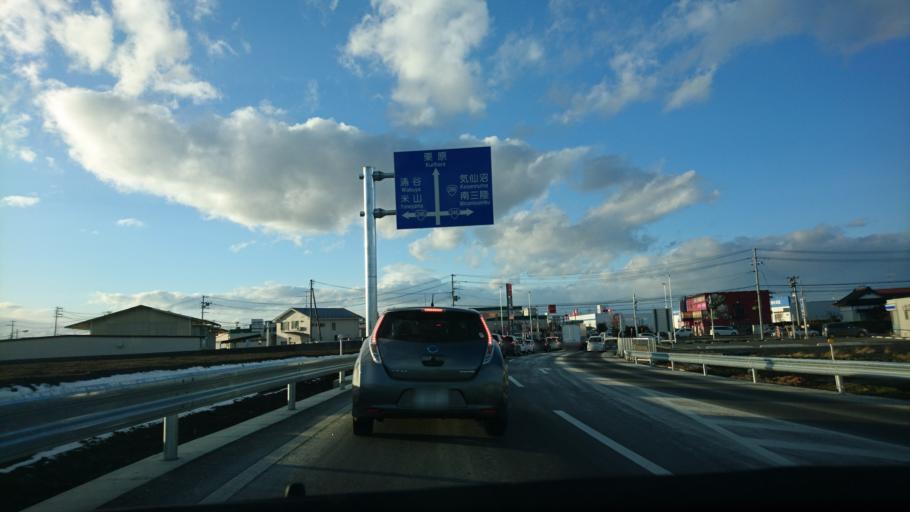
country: JP
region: Miyagi
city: Wakuya
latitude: 38.6961
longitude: 141.2134
